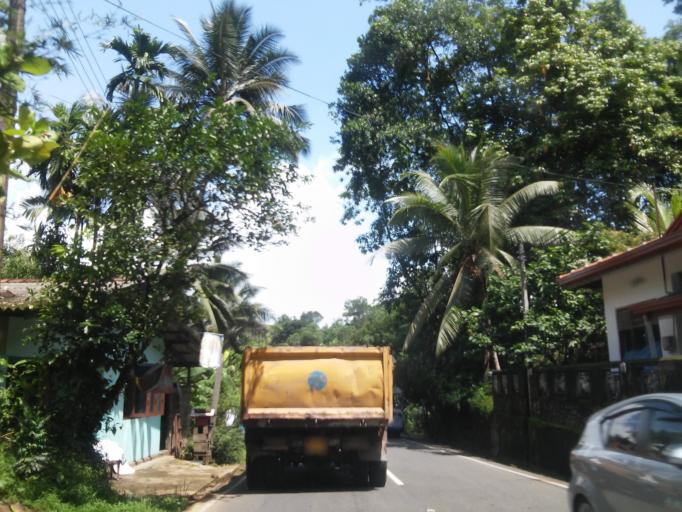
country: LK
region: Sabaragamuwa
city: Ratnapura
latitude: 6.7269
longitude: 80.3311
